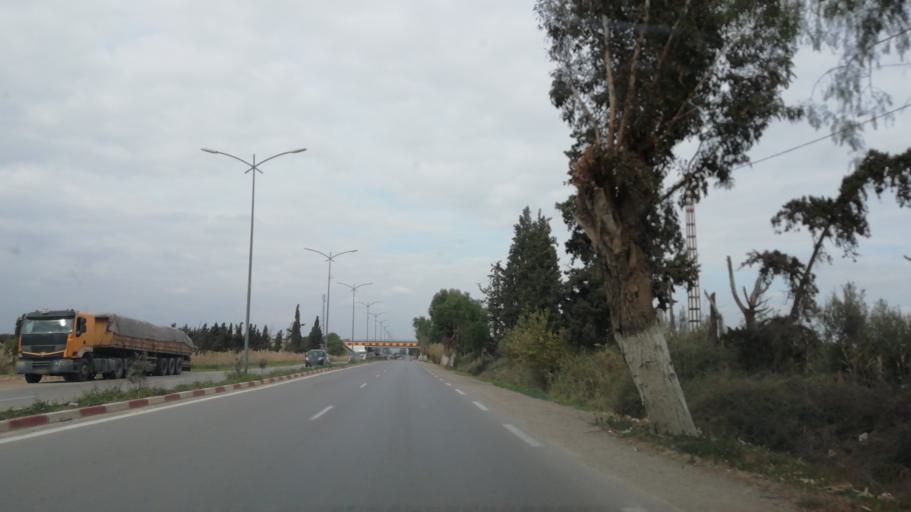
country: DZ
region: Mascara
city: Mascara
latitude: 35.6194
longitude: 0.0623
